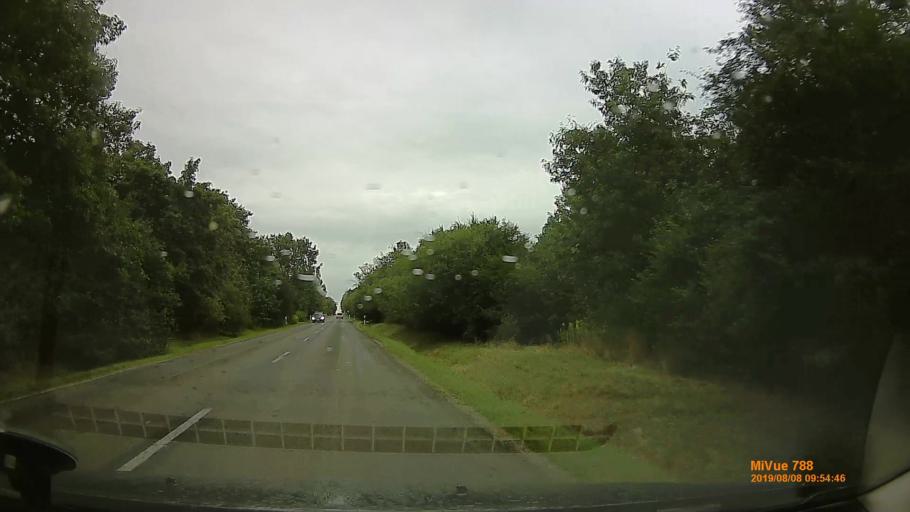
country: HU
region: Vas
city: Vasvar
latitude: 47.0320
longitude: 16.8133
